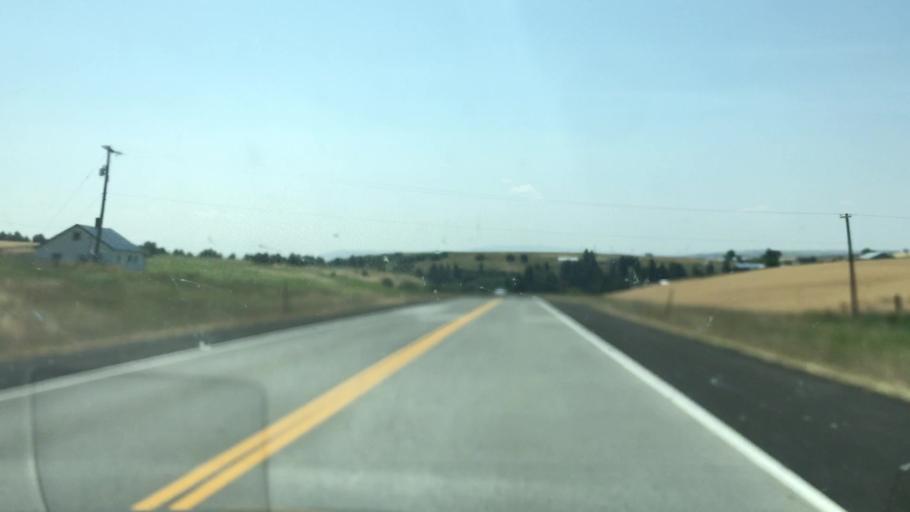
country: US
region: Idaho
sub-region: Lewis County
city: Nezperce
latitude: 46.0531
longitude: -116.3445
